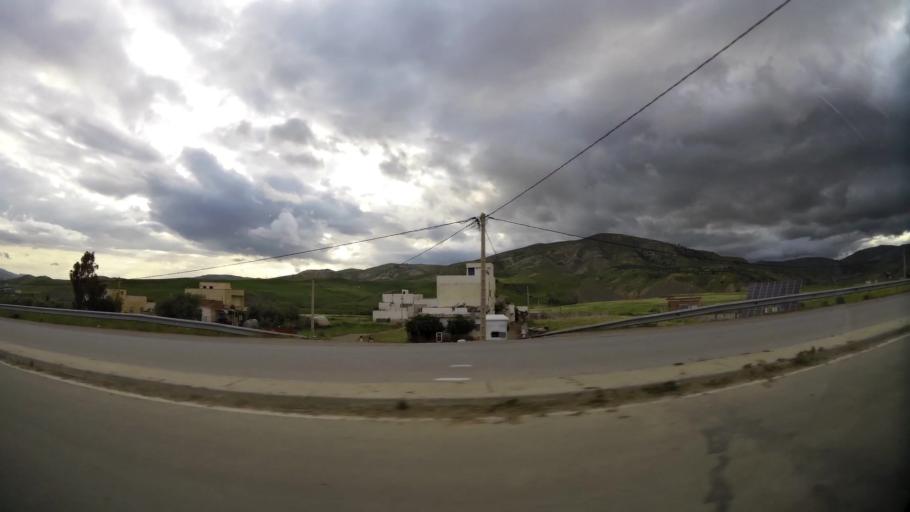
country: MA
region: Taza-Al Hoceima-Taounate
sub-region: Taza
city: Taza
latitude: 34.2640
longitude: -3.9582
